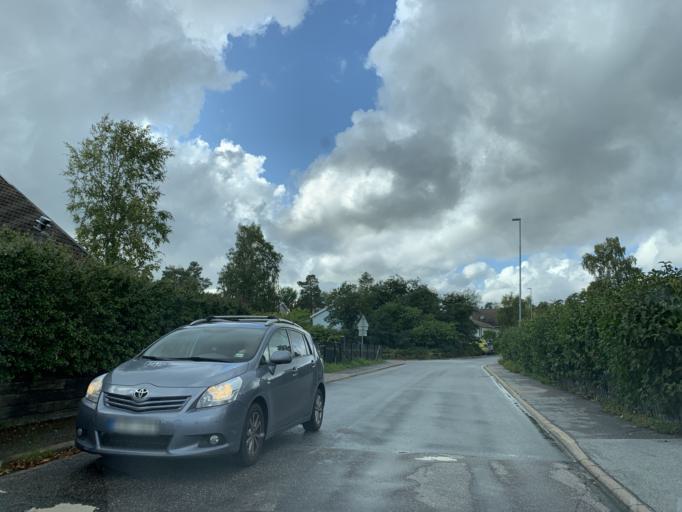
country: SE
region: Stockholm
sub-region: Taby Kommun
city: Taby
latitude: 59.4392
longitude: 18.0217
